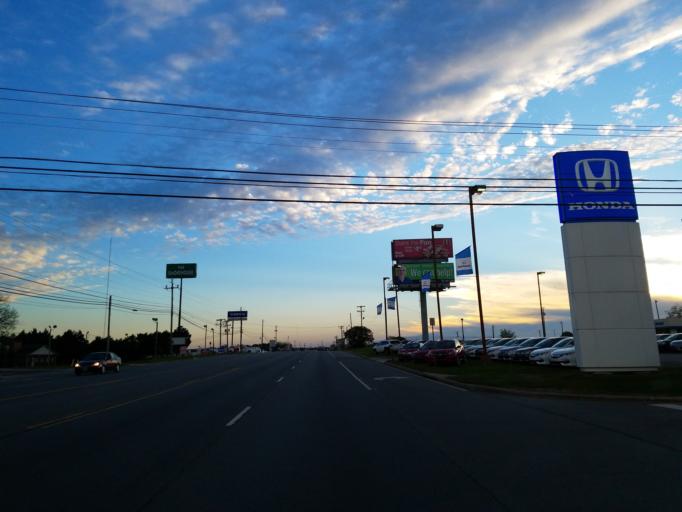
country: US
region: Georgia
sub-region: Tift County
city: Tifton
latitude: 31.4478
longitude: -83.5379
